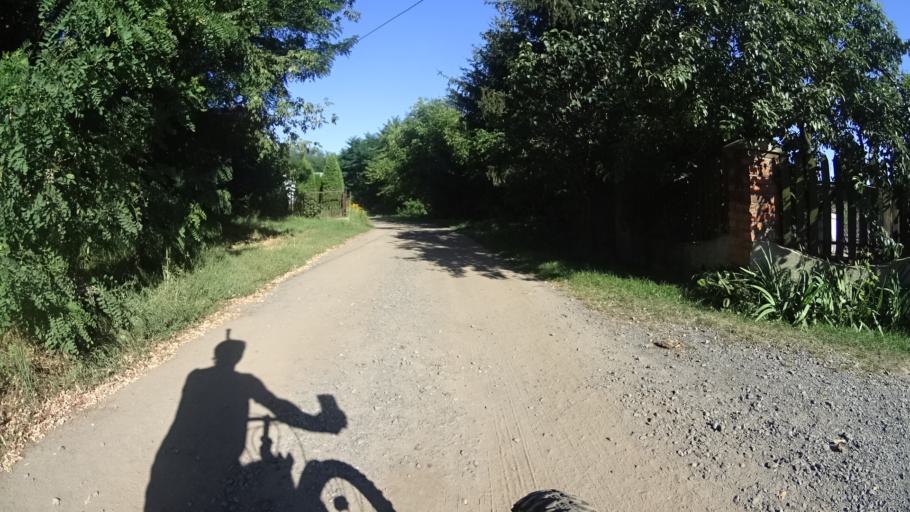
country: PL
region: Masovian Voivodeship
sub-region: Powiat bialobrzeski
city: Wysmierzyce
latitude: 51.6615
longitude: 20.8473
